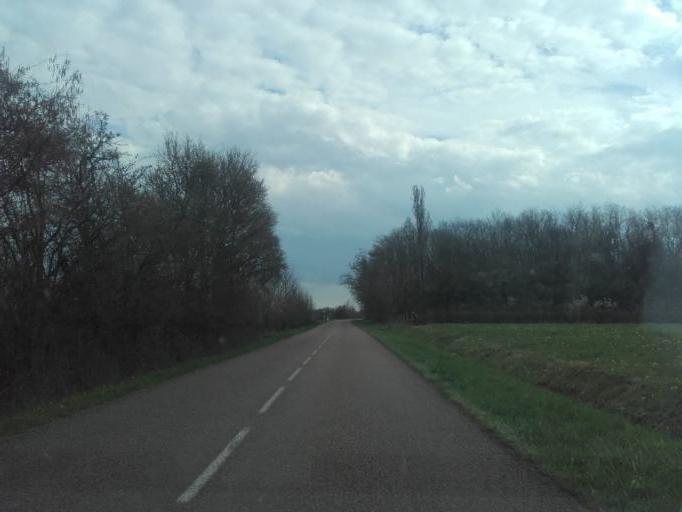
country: FR
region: Bourgogne
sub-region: Departement de la Cote-d'Or
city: Nolay
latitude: 46.9378
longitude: 4.6233
